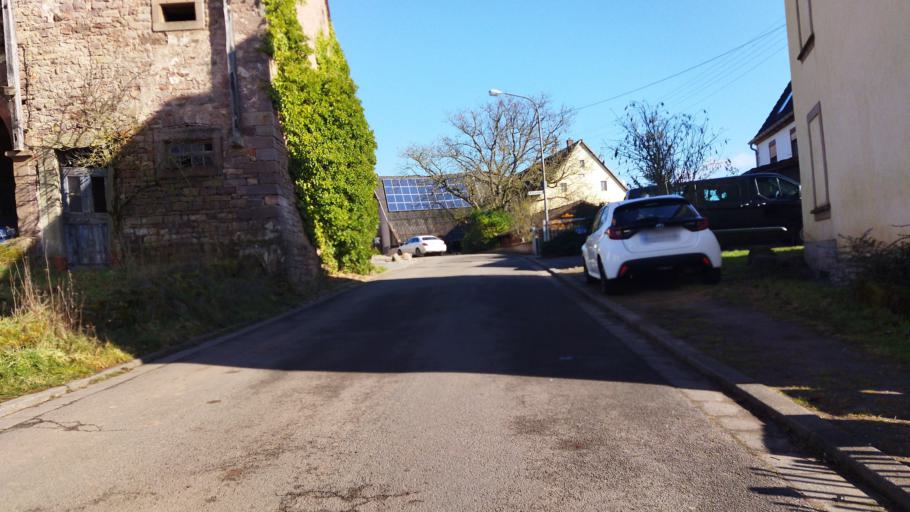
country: DE
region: Rheinland-Pfalz
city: Rehweiler
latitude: 49.4868
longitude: 7.4394
